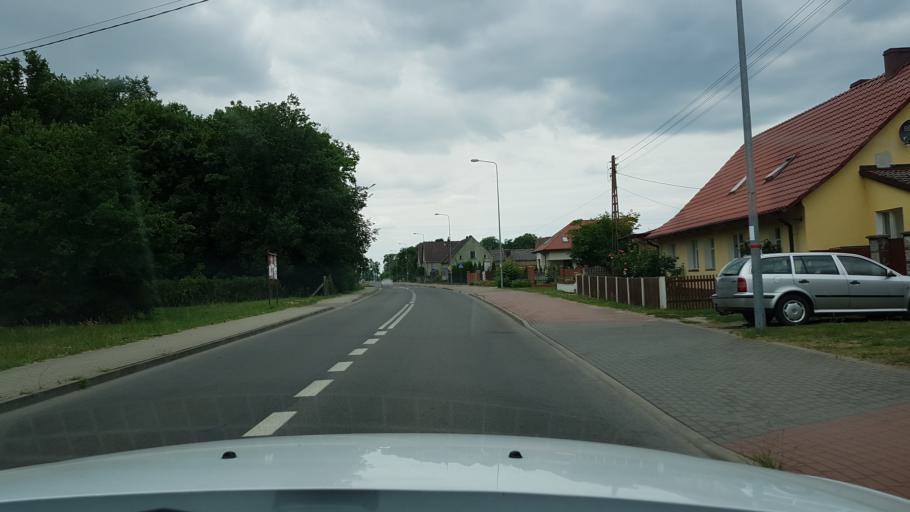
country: PL
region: Lubusz
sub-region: Powiat gorzowski
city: Kostrzyn nad Odra
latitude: 52.6225
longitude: 14.5841
